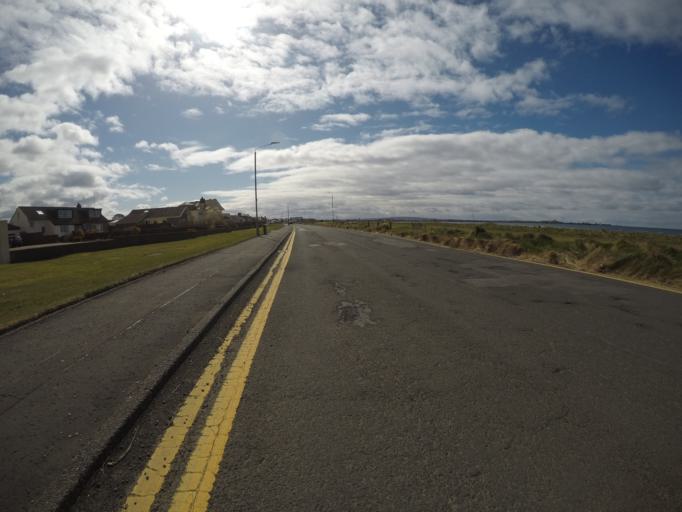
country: GB
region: Scotland
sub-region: South Ayrshire
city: Troon
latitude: 55.5641
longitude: -4.6579
